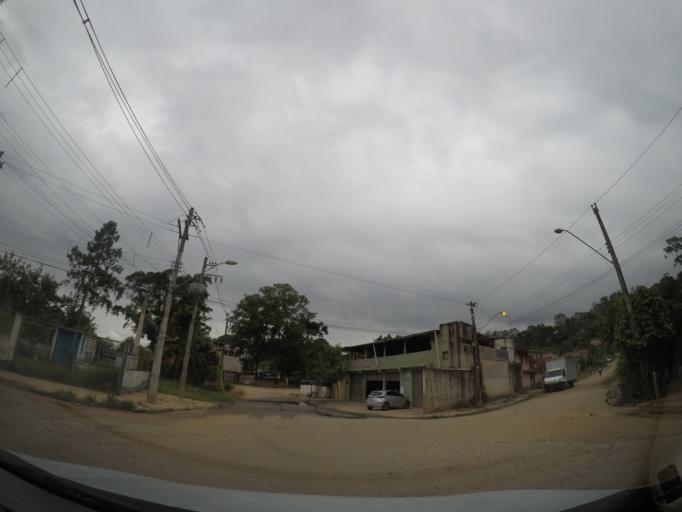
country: BR
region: Sao Paulo
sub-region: Aruja
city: Aruja
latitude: -23.3582
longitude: -46.4067
